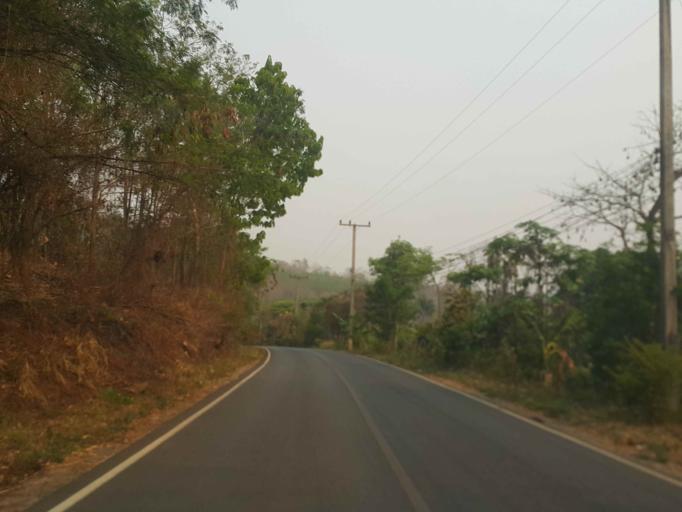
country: TH
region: Chiang Mai
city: Mae Taeng
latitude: 19.1317
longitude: 98.8818
